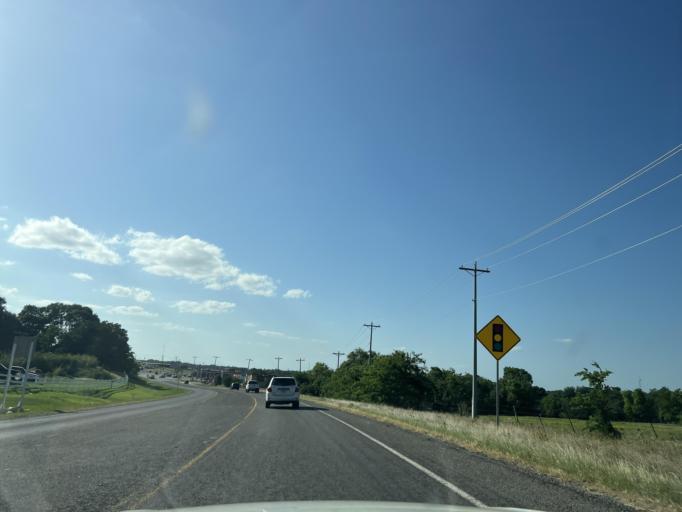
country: US
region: Texas
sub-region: Washington County
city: Brenham
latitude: 30.1756
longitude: -96.3823
